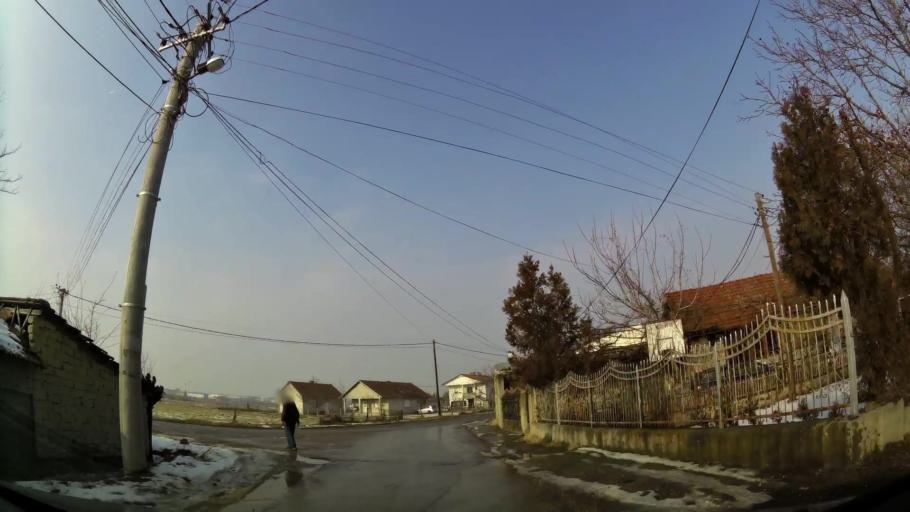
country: MK
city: Kadino
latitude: 41.9739
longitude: 21.5978
